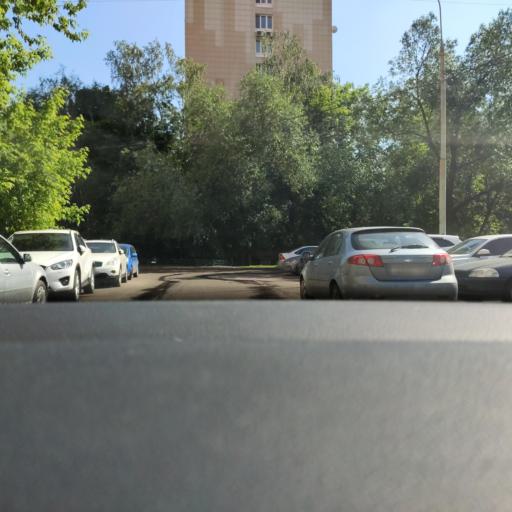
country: RU
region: Moscow
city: Vatutino
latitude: 55.8892
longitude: 37.6553
